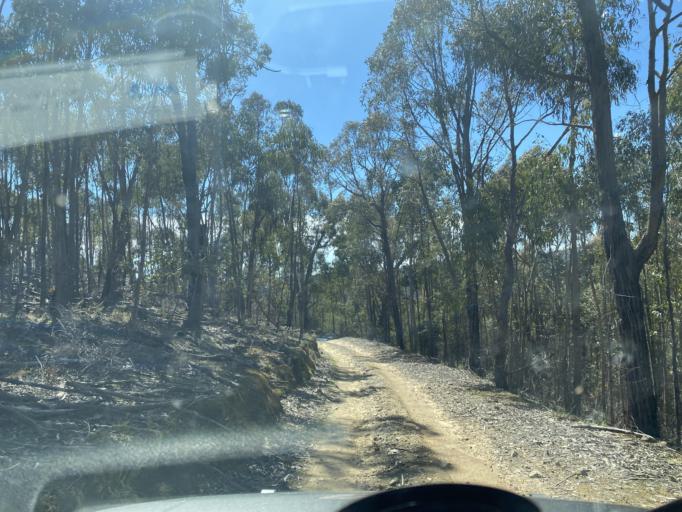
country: AU
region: Victoria
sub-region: Benalla
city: Benalla
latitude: -36.7229
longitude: 146.1819
